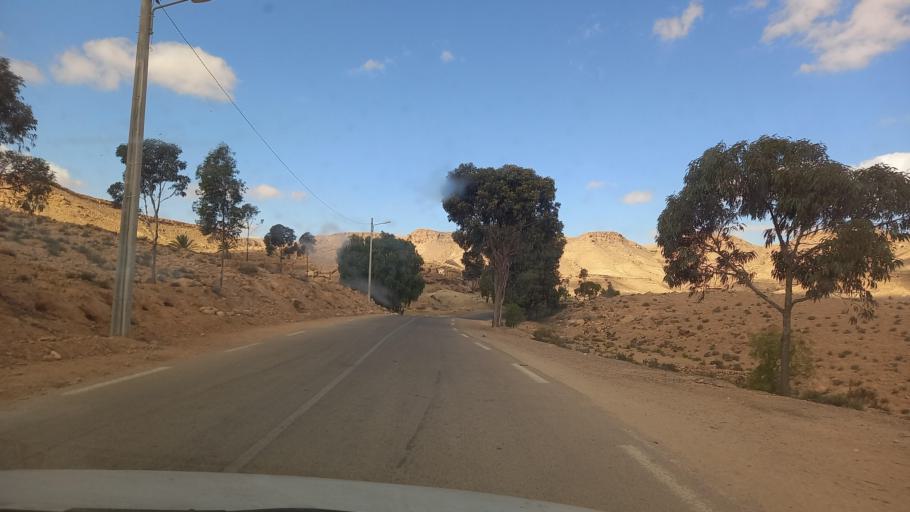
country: TN
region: Tataouine
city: Tataouine
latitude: 32.9161
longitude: 10.2762
